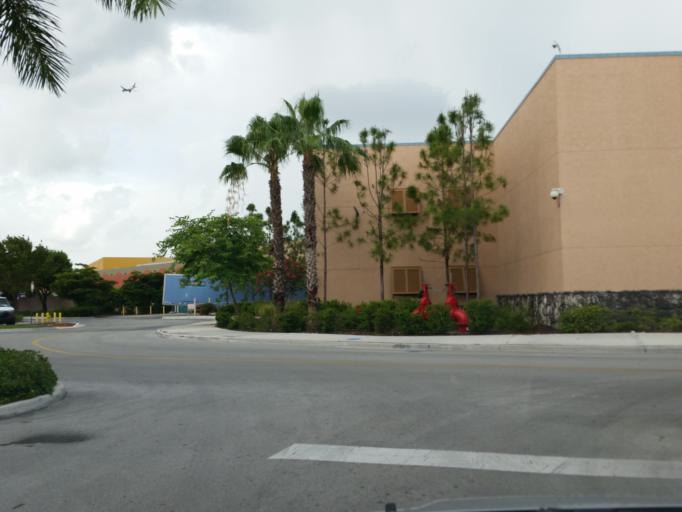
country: US
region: Florida
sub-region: Miami-Dade County
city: Sweetwater
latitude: 25.7896
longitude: -80.3833
